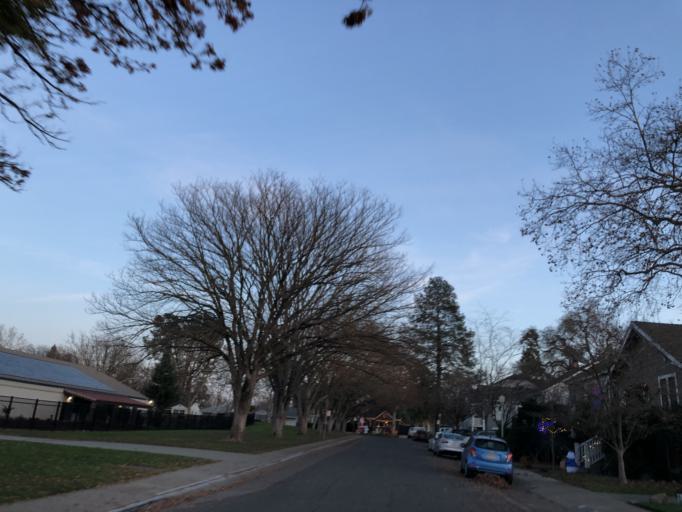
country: US
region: California
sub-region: Sacramento County
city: Sacramento
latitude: 38.5605
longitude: -121.4413
